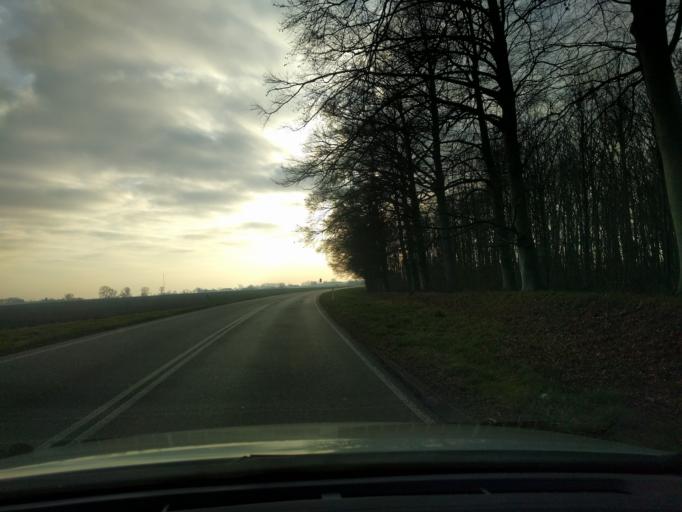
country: DK
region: Zealand
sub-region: Guldborgsund Kommune
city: Stubbekobing
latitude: 54.7762
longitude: 12.0024
